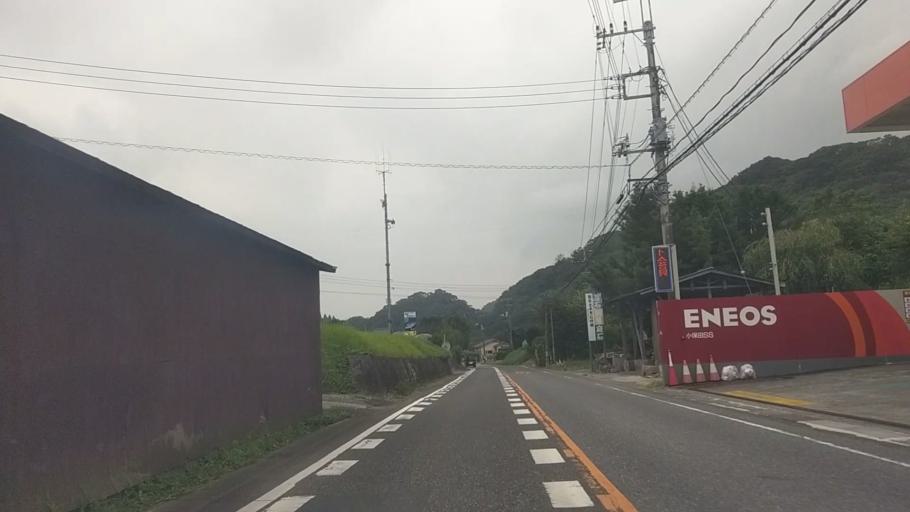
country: JP
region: Chiba
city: Tateyama
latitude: 35.1431
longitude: 139.8778
